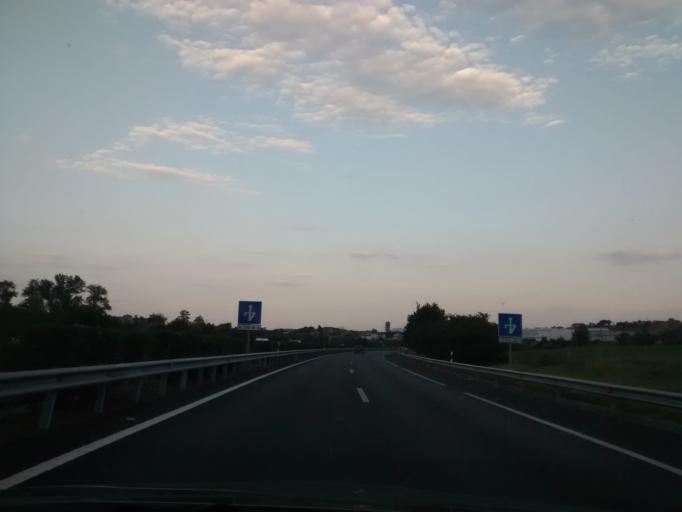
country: ES
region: Cantabria
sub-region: Provincia de Cantabria
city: El Astillero
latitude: 43.4005
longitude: -3.7757
